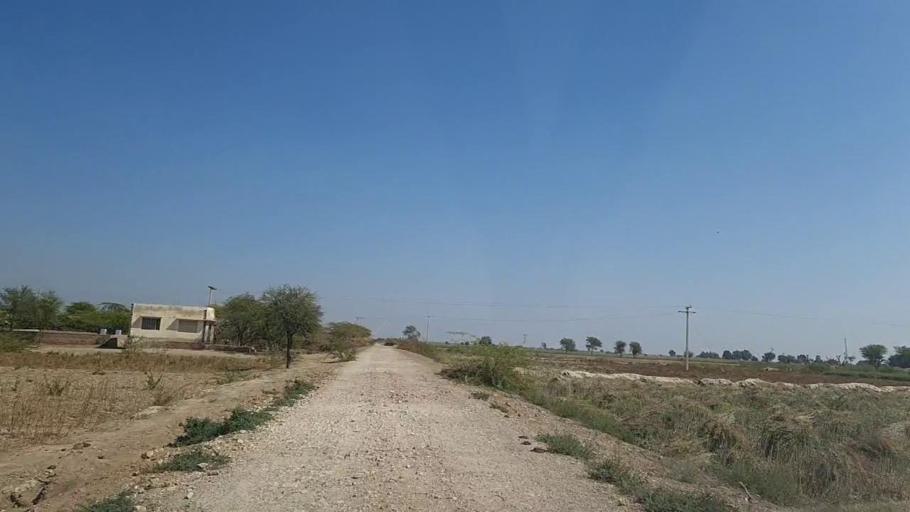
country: PK
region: Sindh
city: Pithoro
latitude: 25.4166
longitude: 69.4084
